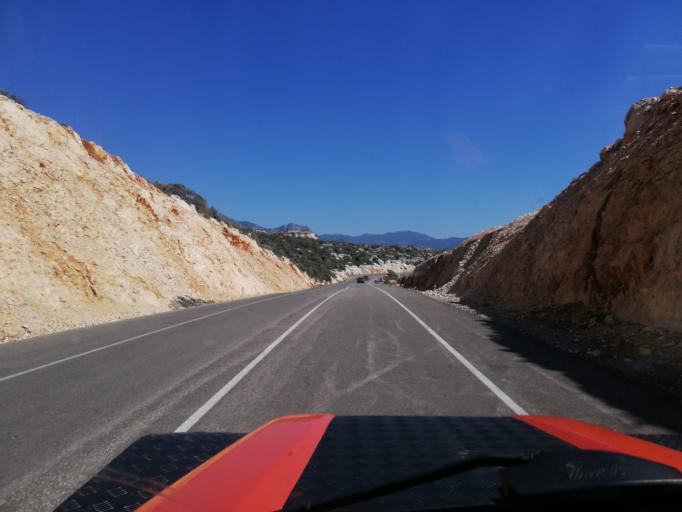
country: GR
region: South Aegean
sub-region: Nomos Dodekanisou
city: Megisti
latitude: 36.2032
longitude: 29.5764
